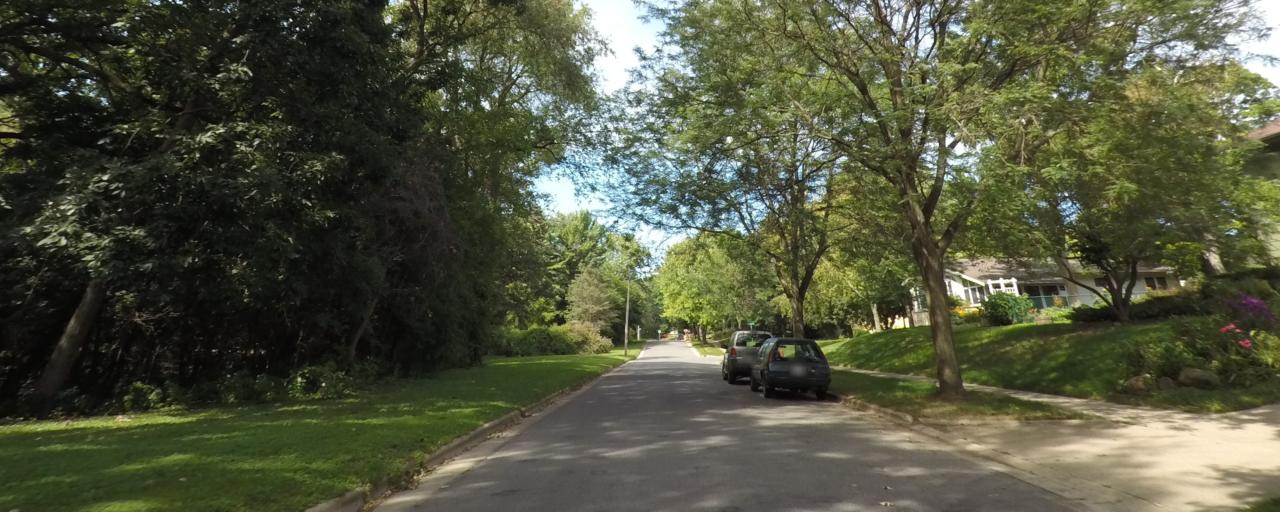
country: US
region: Wisconsin
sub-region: Dane County
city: Shorewood Hills
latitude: 43.0663
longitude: -89.4718
